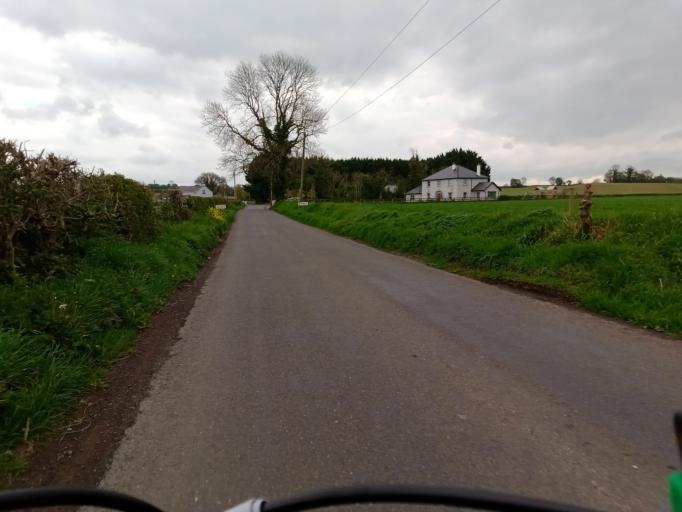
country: IE
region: Leinster
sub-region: Kilkenny
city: Kilkenny
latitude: 52.6183
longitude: -7.2562
